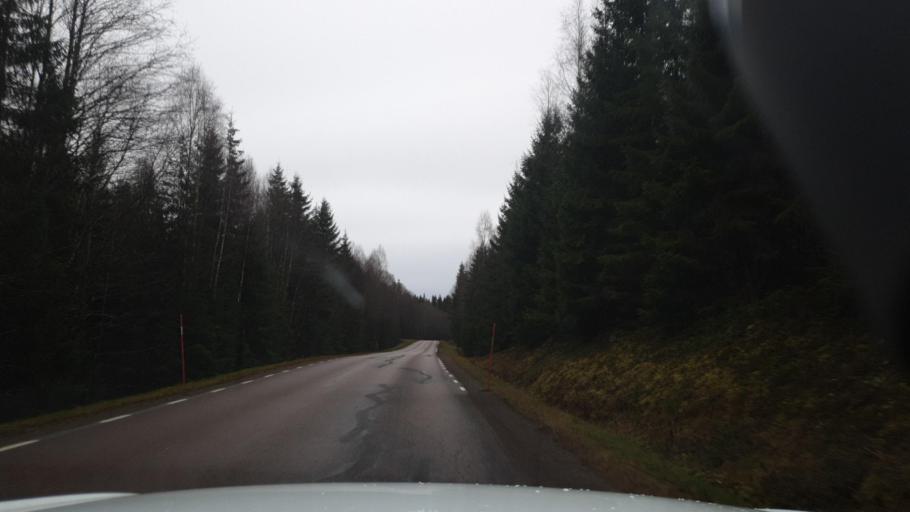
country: SE
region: Vaermland
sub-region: Arvika Kommun
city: Arvika
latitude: 59.6954
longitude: 12.7917
